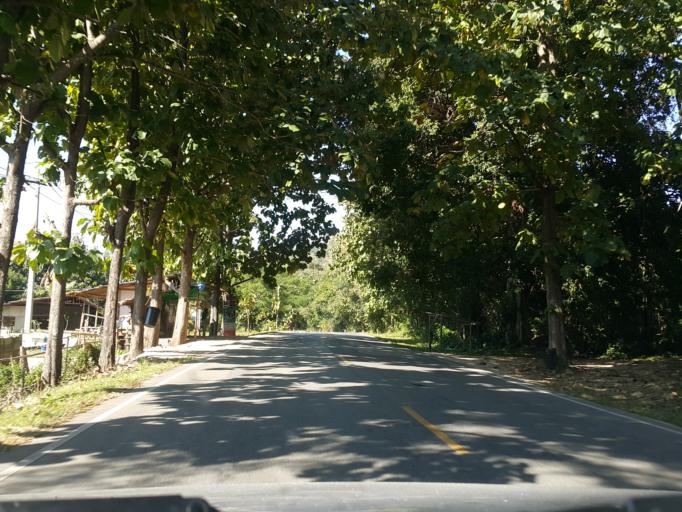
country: TH
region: Mae Hong Son
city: Mae Hi
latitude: 19.2948
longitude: 98.4724
